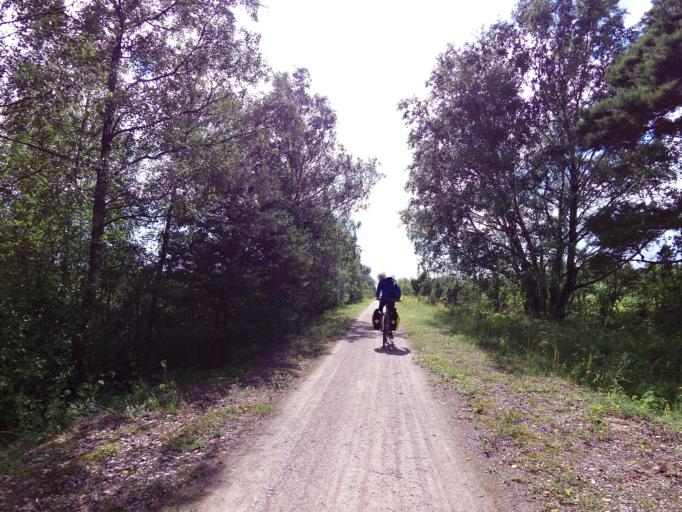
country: EE
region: Laeaene
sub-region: Haapsalu linn
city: Haapsalu
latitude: 58.9114
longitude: 23.4344
